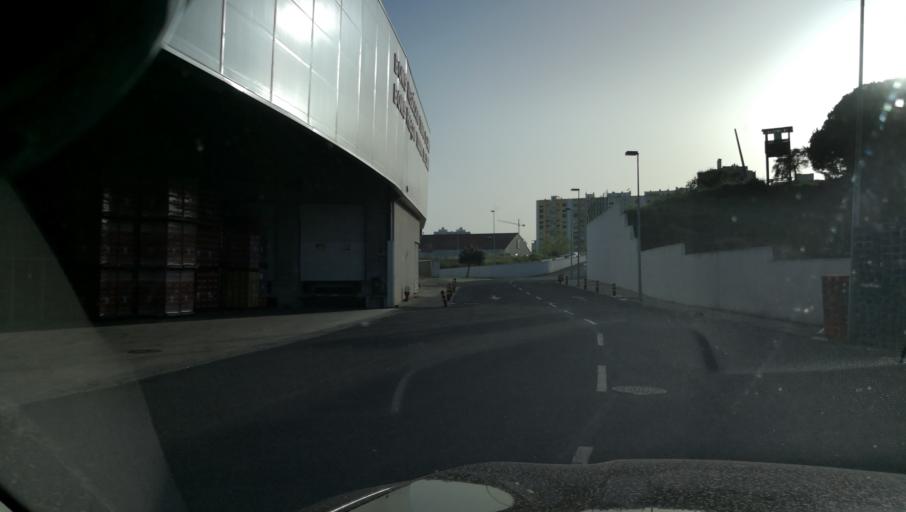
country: PT
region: Setubal
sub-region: Setubal
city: Setubal
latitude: 38.5365
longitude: -8.8645
